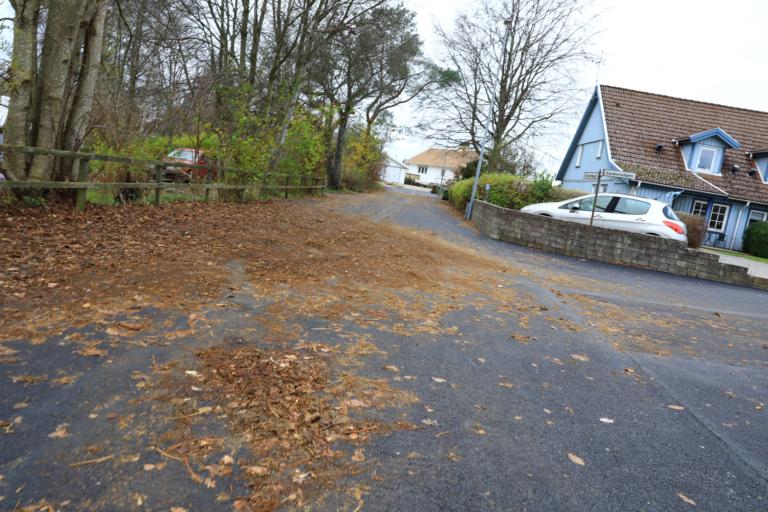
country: SE
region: Halland
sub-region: Varbergs Kommun
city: Tvaaker
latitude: 57.0414
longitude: 12.4012
